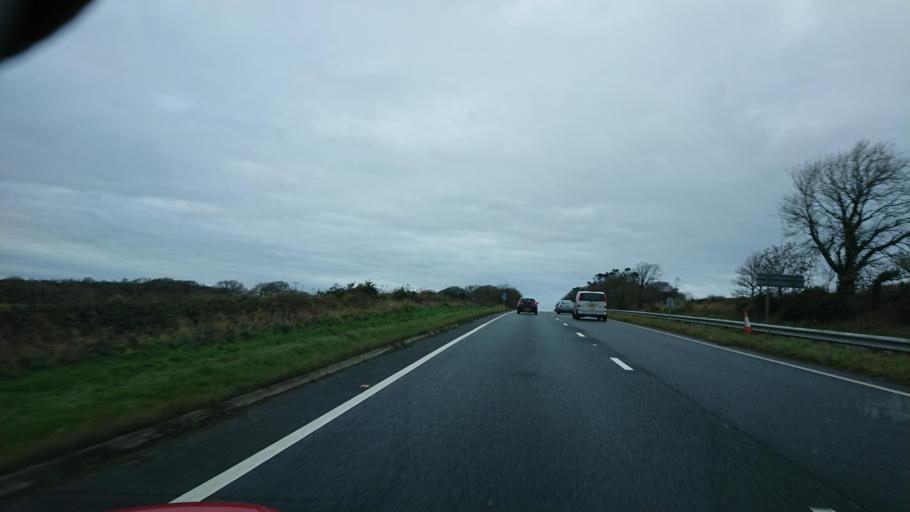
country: GB
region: England
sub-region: Cornwall
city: Liskeard
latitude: 50.4244
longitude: -4.4147
